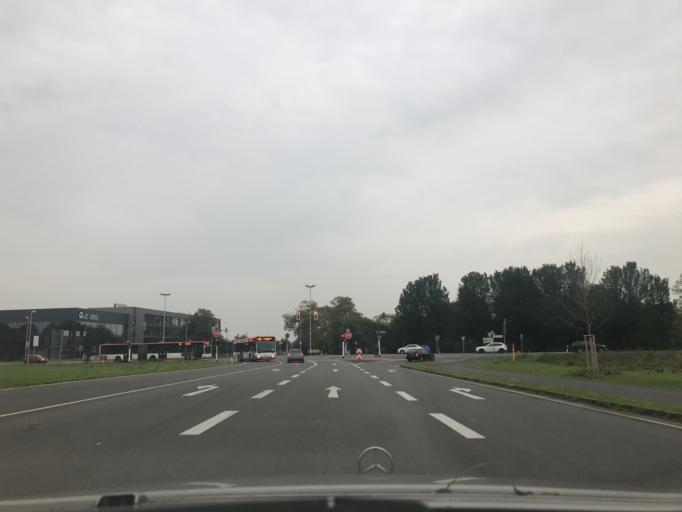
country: DE
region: North Rhine-Westphalia
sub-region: Regierungsbezirk Dusseldorf
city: Willich
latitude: 51.2955
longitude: 6.5534
